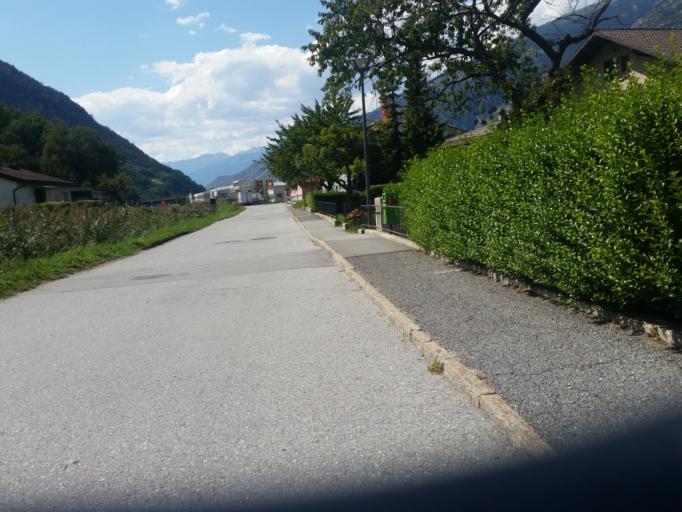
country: CH
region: Valais
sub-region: Raron District
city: Raron
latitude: 46.3043
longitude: 7.7995
